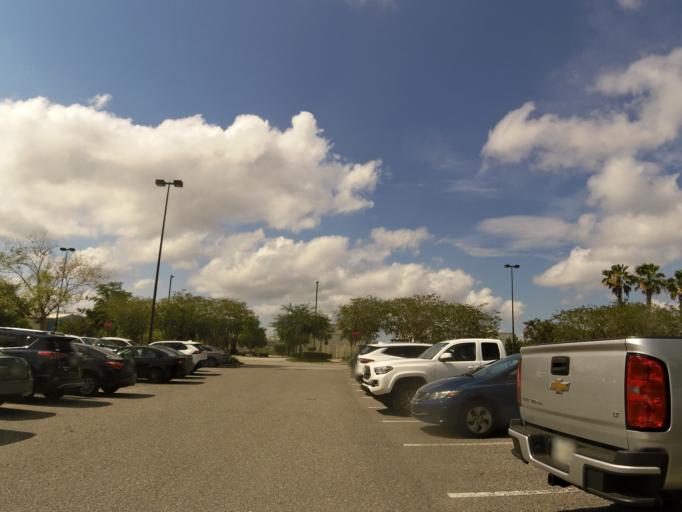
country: US
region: Florida
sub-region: Duval County
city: Jacksonville Beach
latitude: 30.2532
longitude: -81.5314
